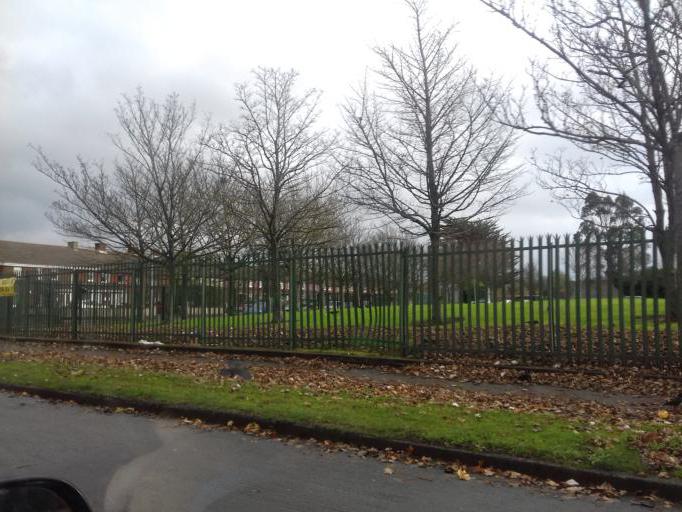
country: IE
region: Leinster
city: Raheny
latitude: 53.3837
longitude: -6.1839
